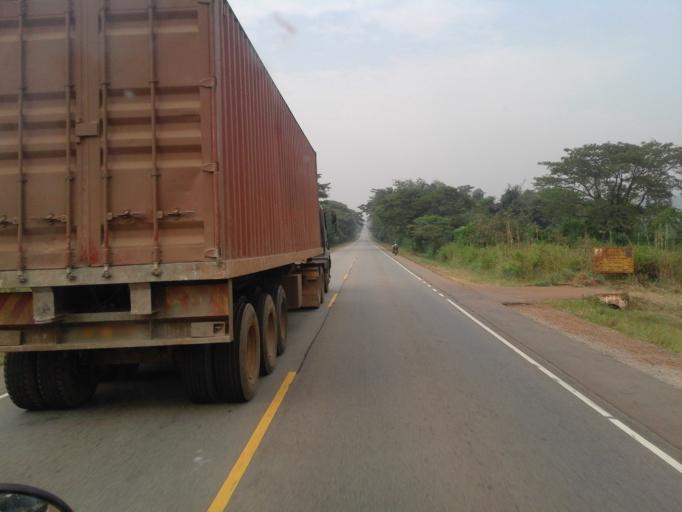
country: UG
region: Eastern Region
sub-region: Busia District
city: Busia
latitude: 0.5304
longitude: 33.9831
